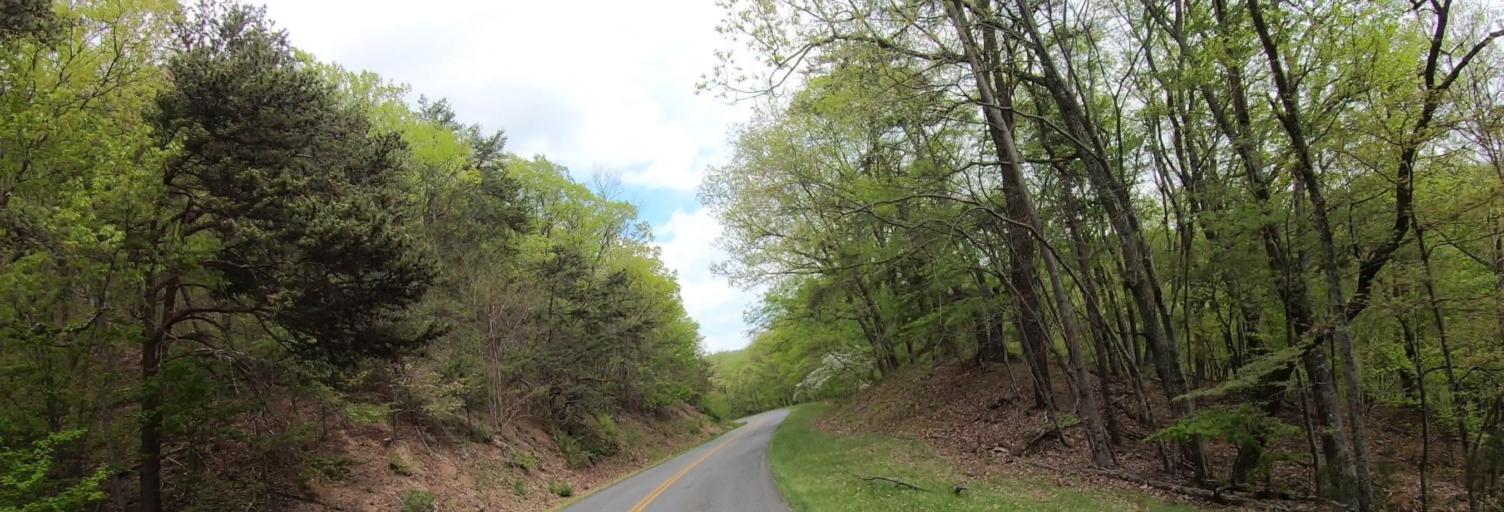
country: US
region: Virginia
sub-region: Botetourt County
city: Blue Ridge
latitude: 37.4047
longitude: -79.8240
